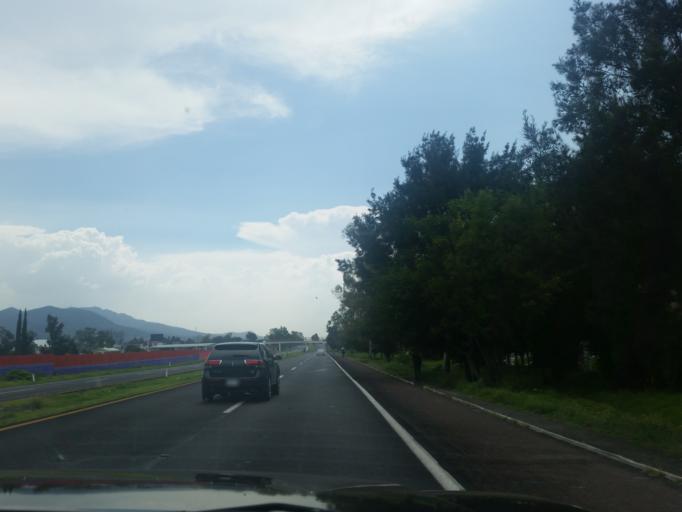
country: MX
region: Mexico
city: Santo Tomas Chiconautla
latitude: 19.6229
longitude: -98.9941
